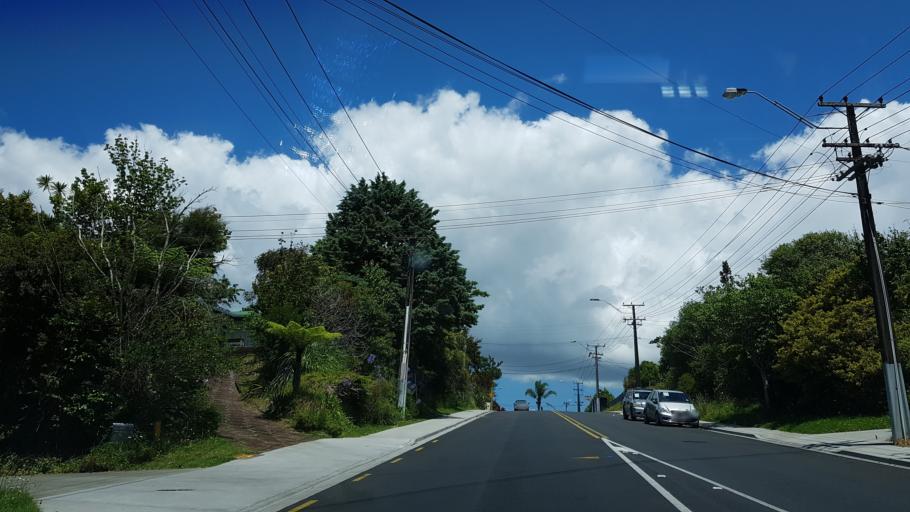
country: NZ
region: Auckland
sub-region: Auckland
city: North Shore
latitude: -36.7888
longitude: 174.6969
